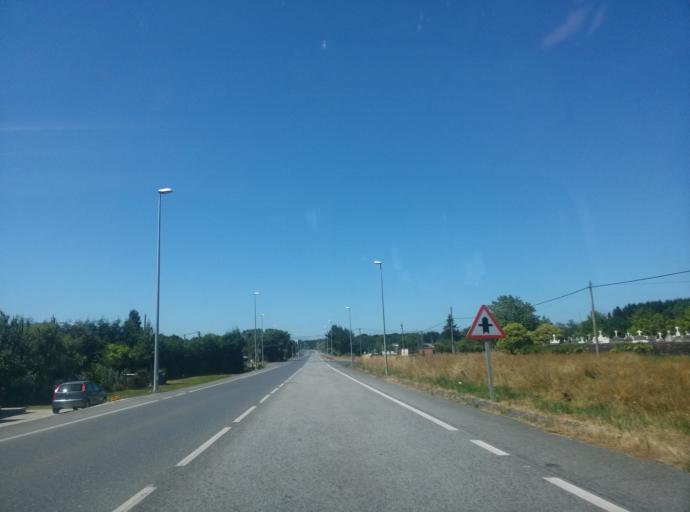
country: ES
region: Galicia
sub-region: Provincia de Lugo
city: Mos
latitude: 43.1292
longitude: -7.4882
